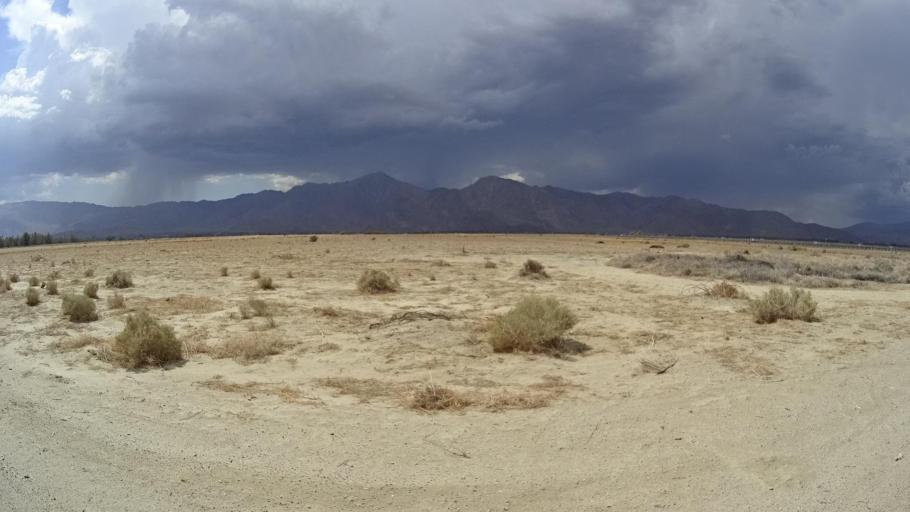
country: US
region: California
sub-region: San Diego County
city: Borrego Springs
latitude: 33.2853
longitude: -116.3488
